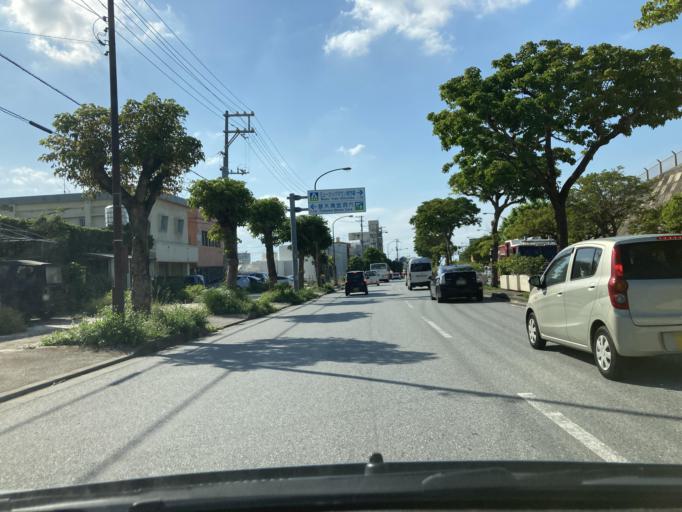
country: JP
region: Okinawa
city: Chatan
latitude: 26.2960
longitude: 127.7827
